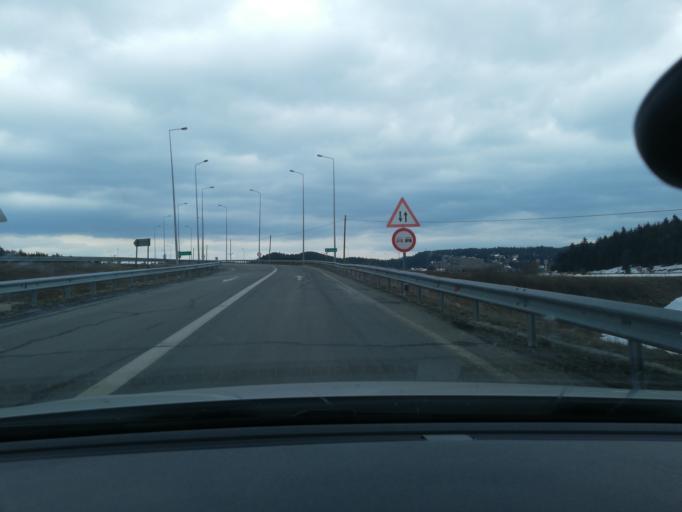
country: TR
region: Bolu
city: Gerede
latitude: 40.6102
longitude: 32.2519
